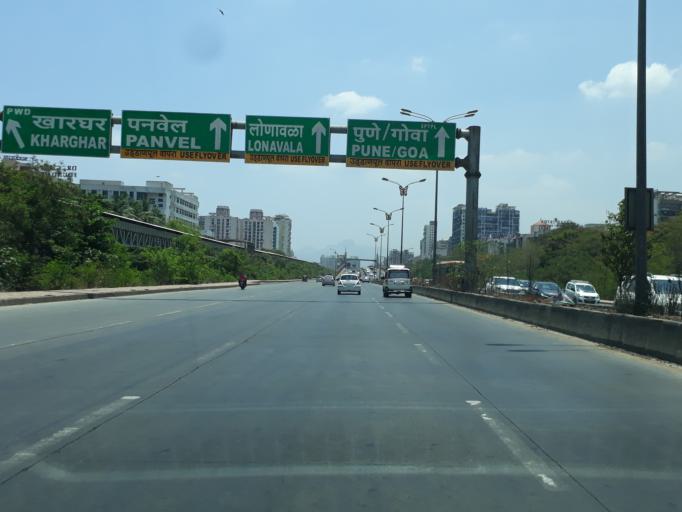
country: IN
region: Maharashtra
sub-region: Thane
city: Artist Village
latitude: 19.0293
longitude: 73.0616
